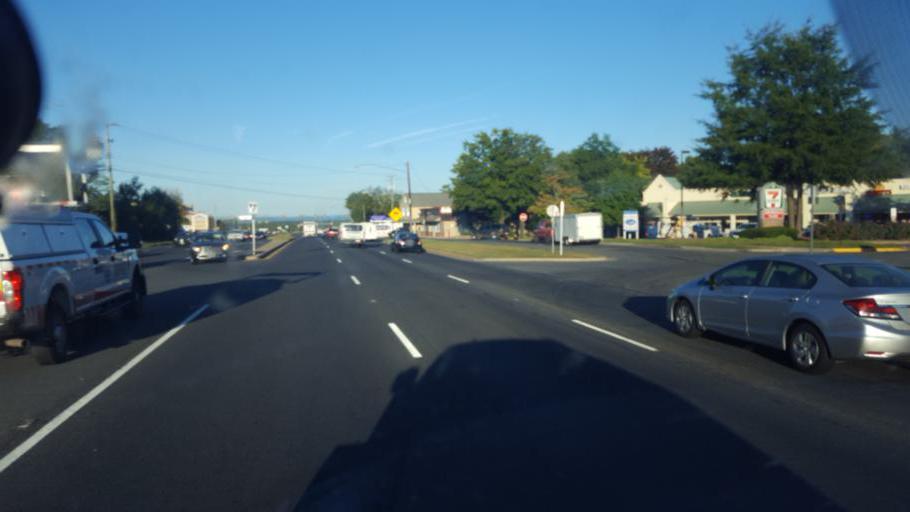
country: US
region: Virginia
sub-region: Fairfax County
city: Centreville
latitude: 38.8389
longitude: -77.4255
